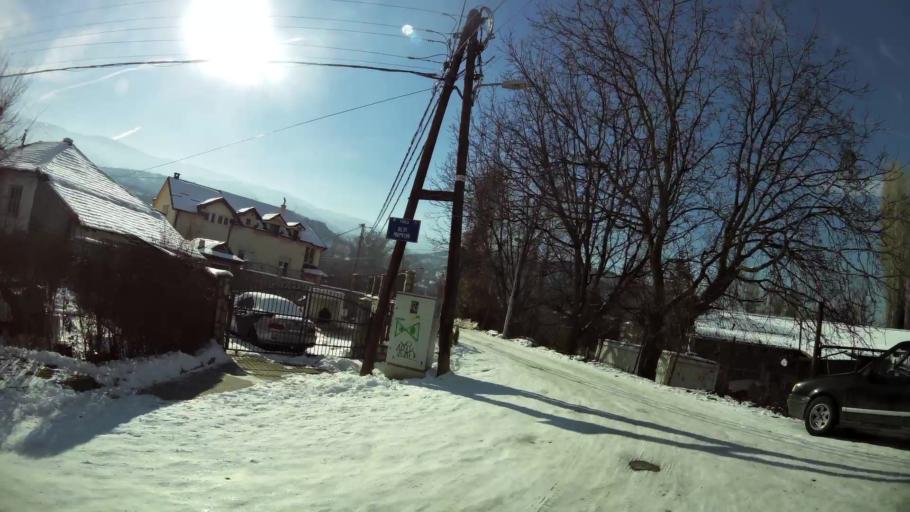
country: MK
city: Krushopek
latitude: 42.0003
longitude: 21.3688
